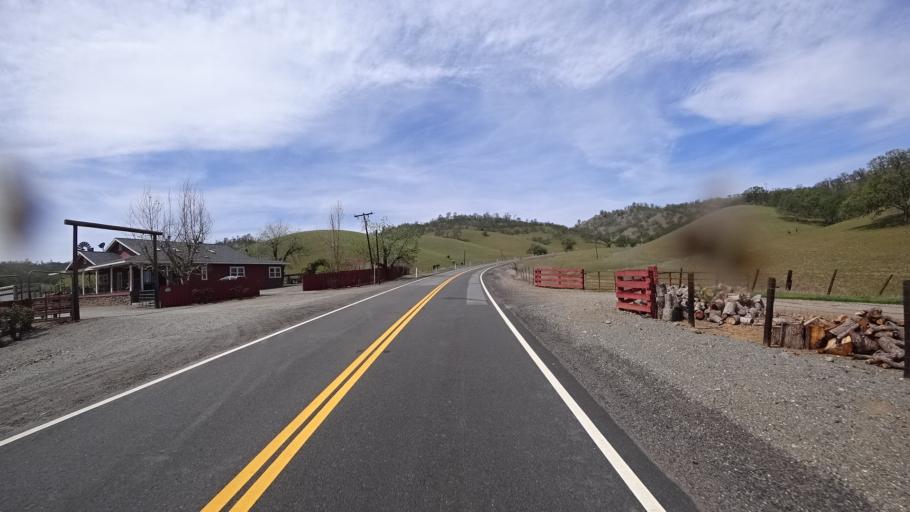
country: US
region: California
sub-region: Glenn County
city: Willows
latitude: 39.5964
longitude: -122.4890
